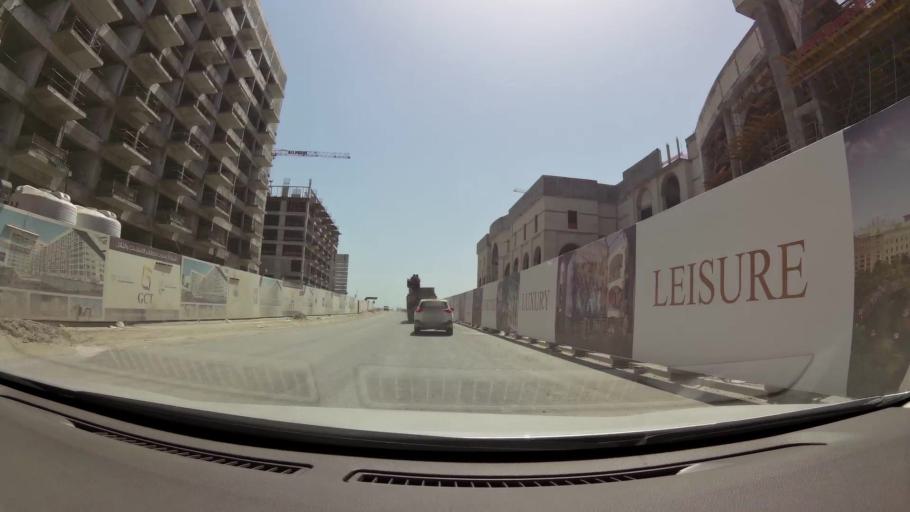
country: QA
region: Baladiyat Umm Salal
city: Umm Salal Muhammad
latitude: 25.4057
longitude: 51.5217
